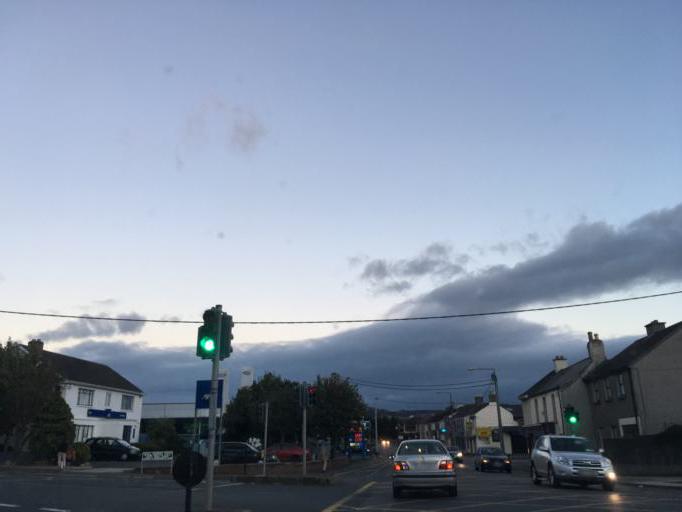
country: IE
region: Leinster
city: Little Bray
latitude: 53.2108
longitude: -6.1172
